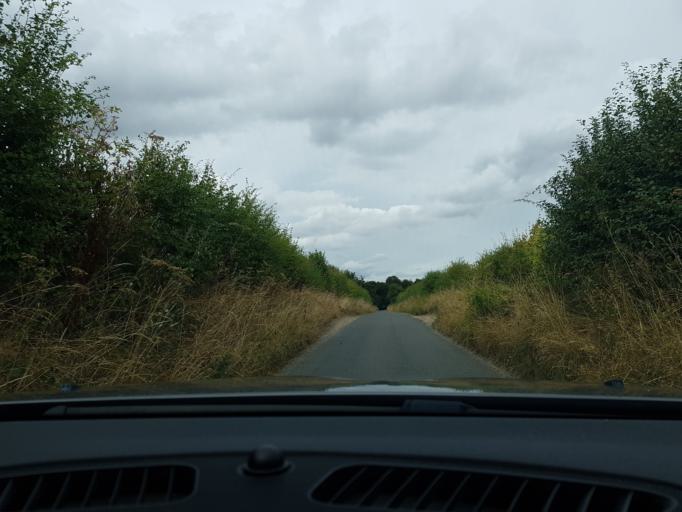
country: GB
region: England
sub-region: West Berkshire
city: Kintbury
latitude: 51.4174
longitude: -1.4663
